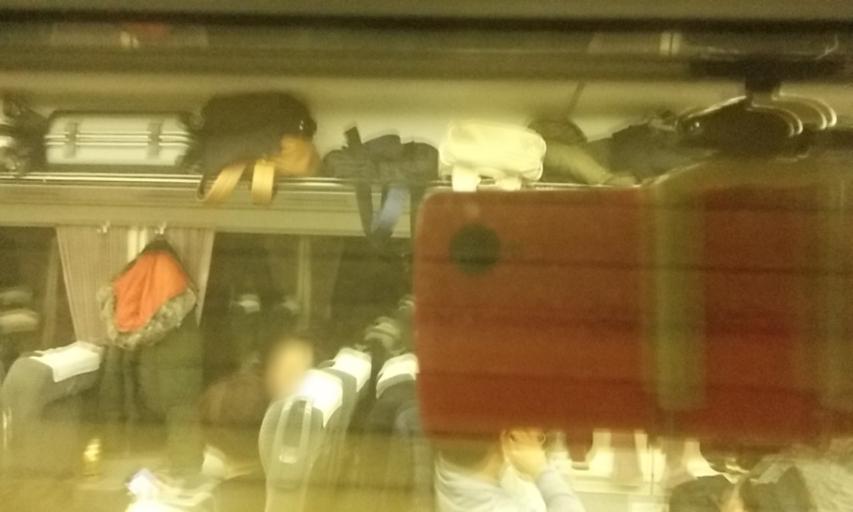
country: JP
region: Nagano
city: Ina
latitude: 35.8997
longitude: 137.7688
